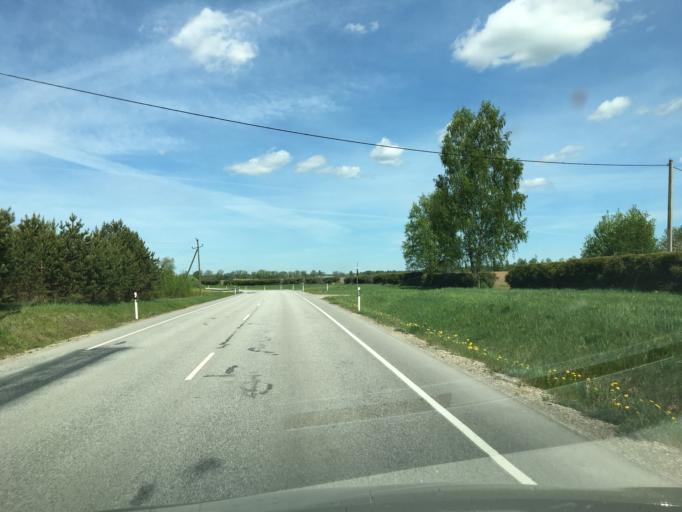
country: EE
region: Vorumaa
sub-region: Antsla vald
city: Vana-Antsla
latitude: 57.8959
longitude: 26.2895
